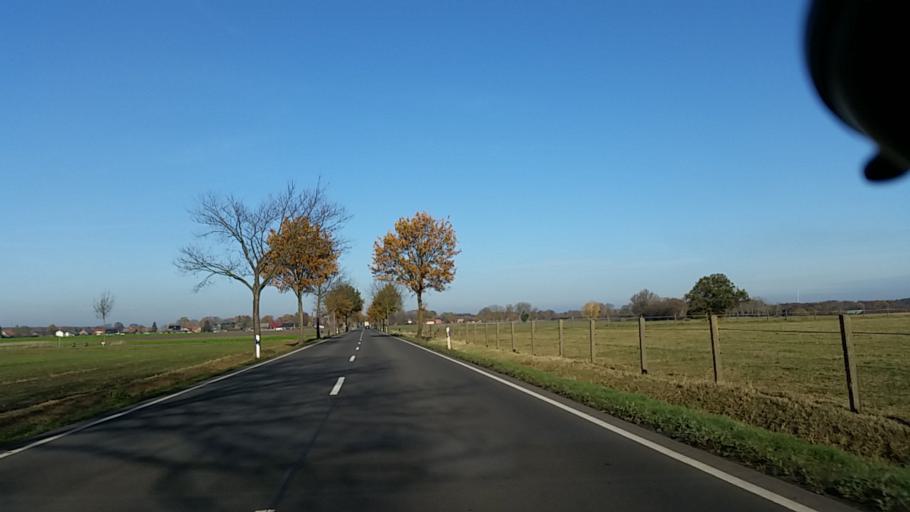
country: DE
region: Saxony-Anhalt
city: Jubar
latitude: 52.6631
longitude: 10.8530
